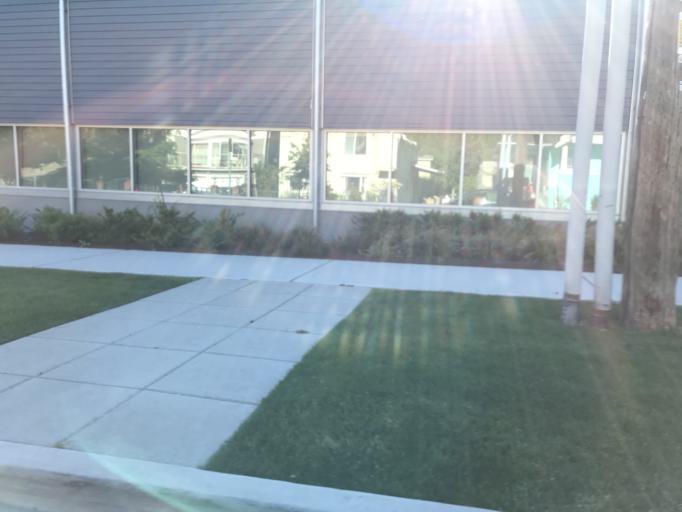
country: US
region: Washington
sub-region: King County
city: Seattle
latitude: 47.5880
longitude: -122.3073
